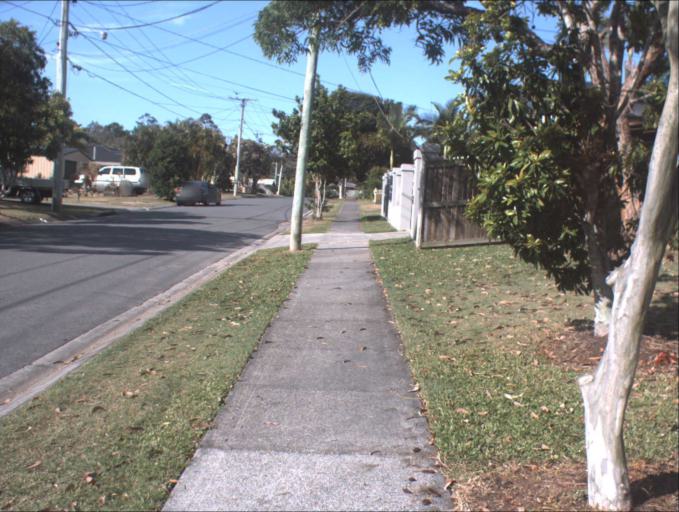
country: AU
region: Queensland
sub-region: Logan
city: Slacks Creek
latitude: -27.6595
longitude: 153.1805
